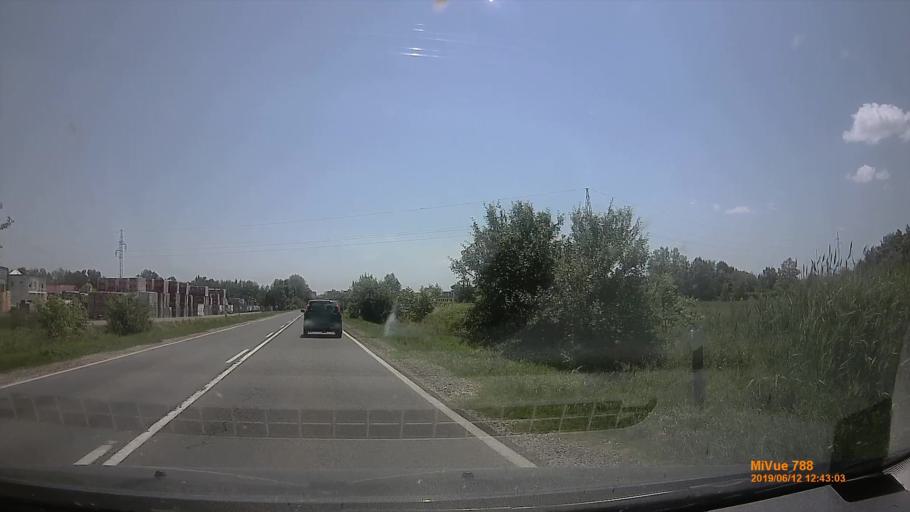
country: HU
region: Bacs-Kiskun
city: Kiskunfelegyhaza
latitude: 46.7321
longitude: 19.8437
